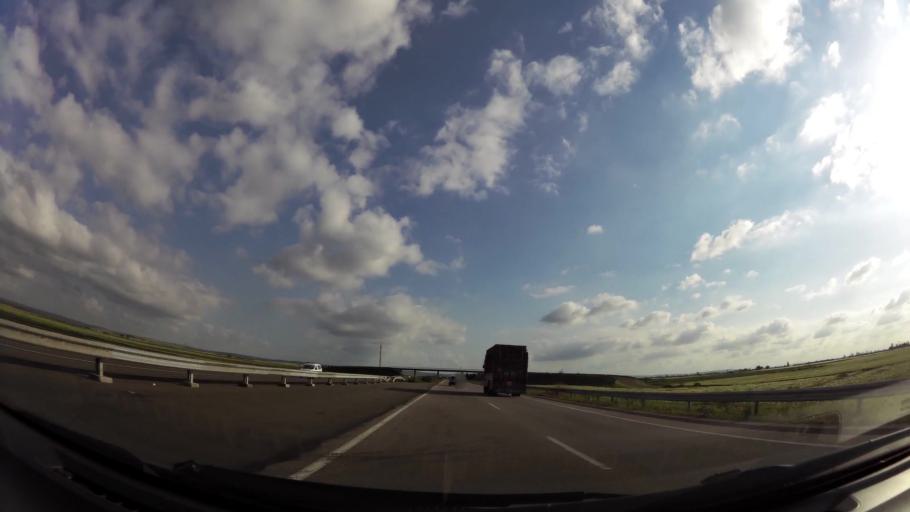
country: MA
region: Chaouia-Ouardigha
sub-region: Settat Province
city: Berrechid
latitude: 33.1492
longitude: -7.5728
